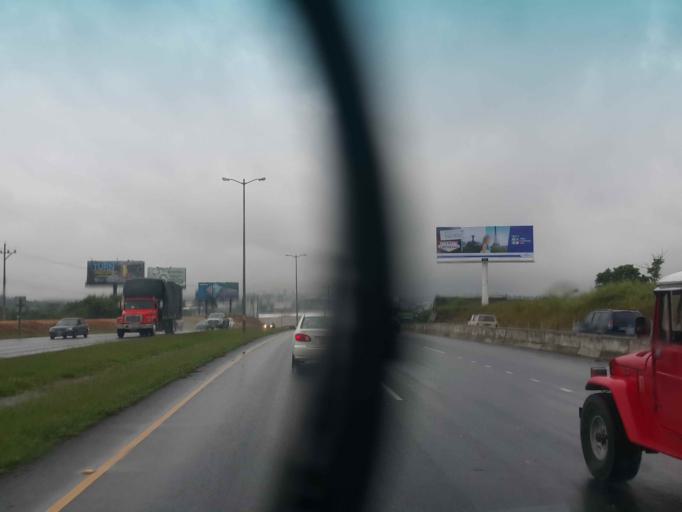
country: CR
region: San Jose
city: San Rafael
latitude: 9.9478
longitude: -84.1553
